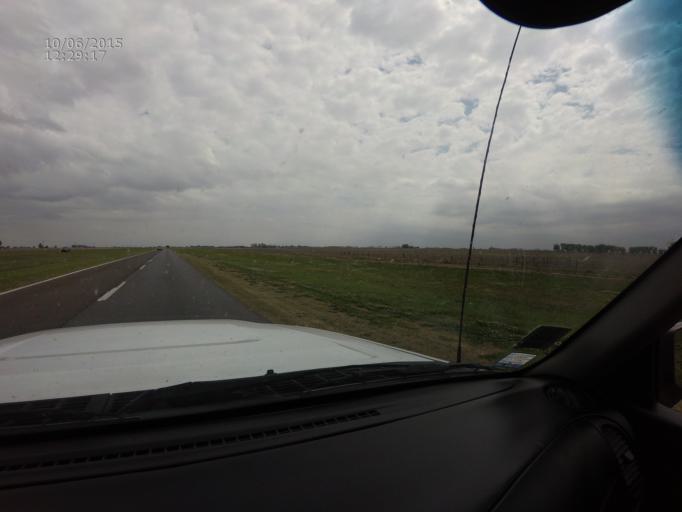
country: AR
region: Santa Fe
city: Carcarana
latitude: -32.8929
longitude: -61.0773
